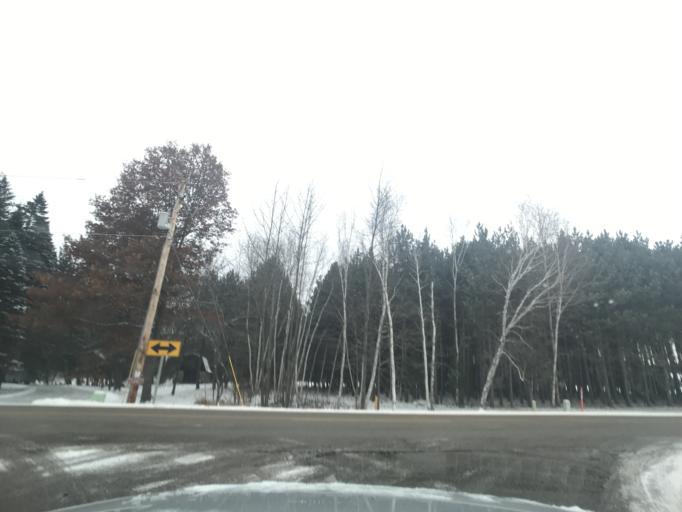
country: US
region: Wisconsin
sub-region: Brown County
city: Suamico
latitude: 44.6919
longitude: -88.1008
